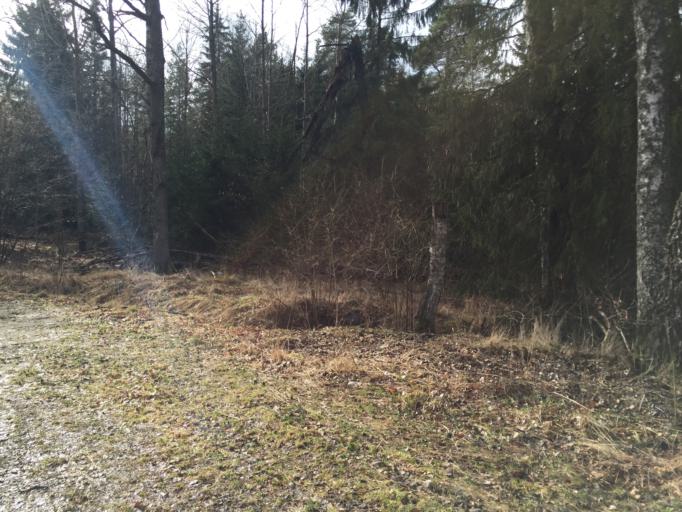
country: SE
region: Stockholm
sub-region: Salems Kommun
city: Ronninge
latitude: 59.2216
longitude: 17.7388
